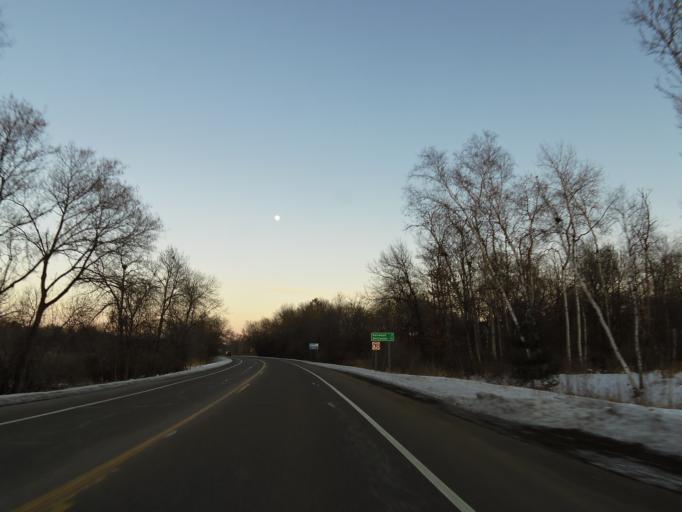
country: US
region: Minnesota
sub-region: Ramsey County
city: White Bear Lake
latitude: 45.0934
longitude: -93.0033
